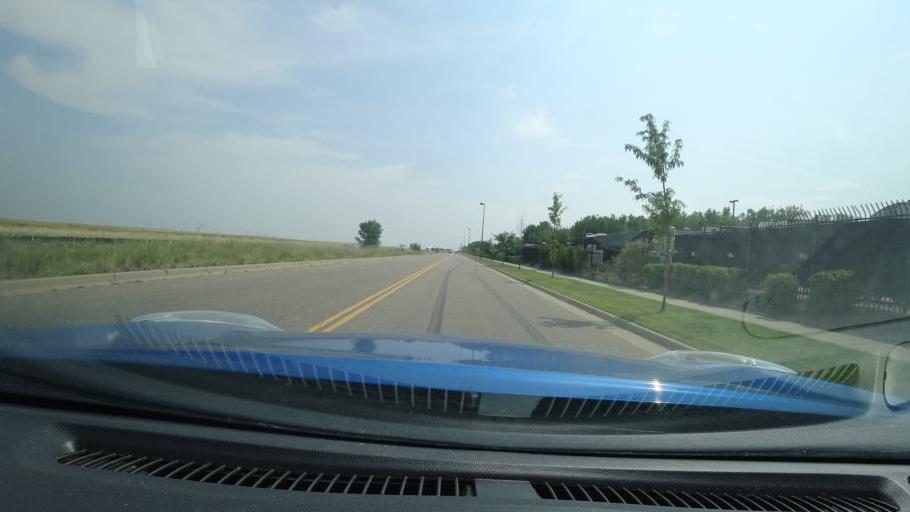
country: US
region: Colorado
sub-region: Adams County
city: Aurora
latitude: 39.7772
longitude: -104.7346
